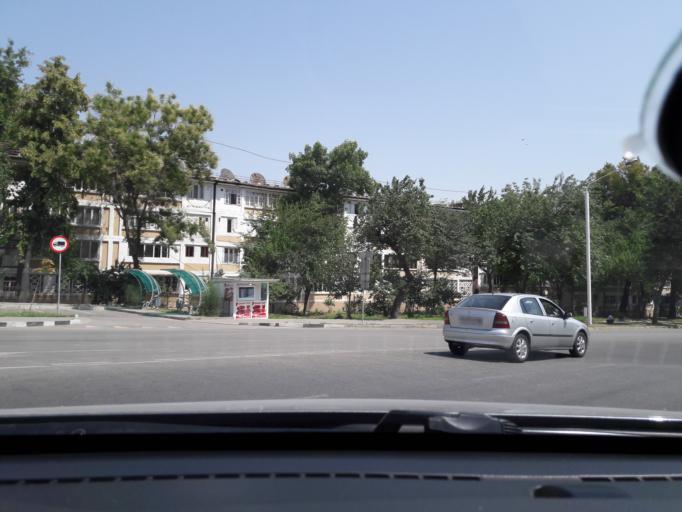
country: TJ
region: Dushanbe
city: Dushanbe
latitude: 38.5895
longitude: 68.7329
